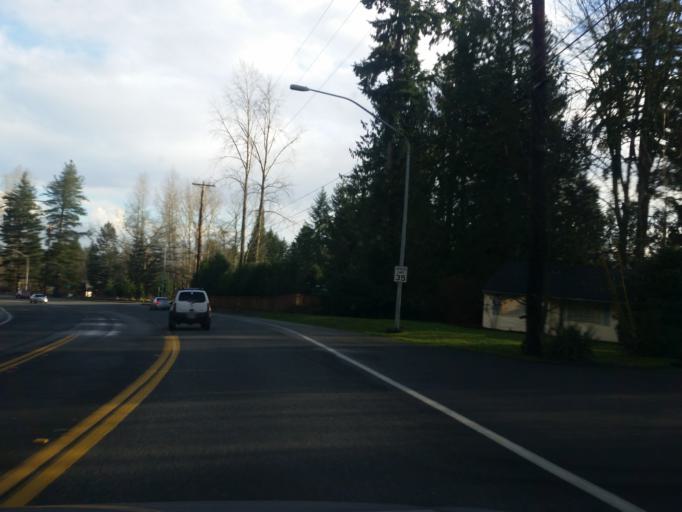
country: US
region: Washington
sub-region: Snohomish County
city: Martha Lake
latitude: 47.8104
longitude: -122.2252
